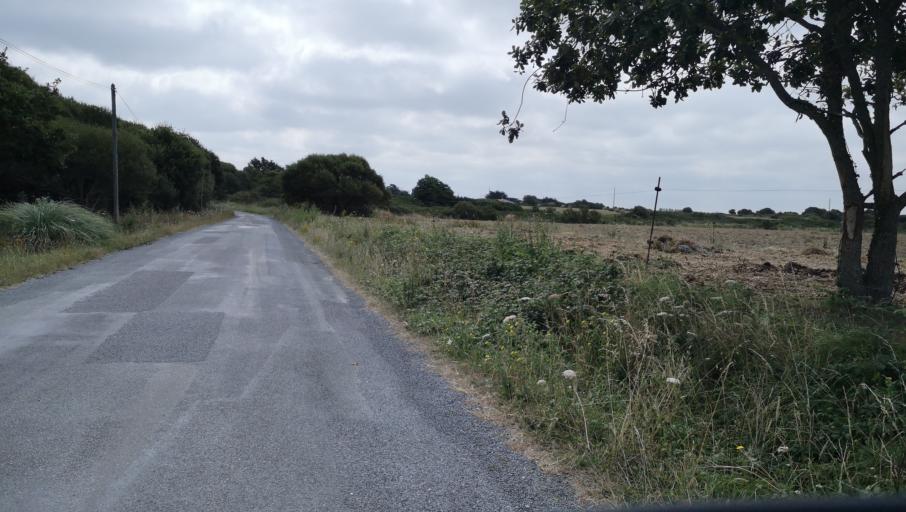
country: FR
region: Pays de la Loire
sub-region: Departement de la Vendee
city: Bretignolles-sur-Mer
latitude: 46.5967
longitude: -1.8242
